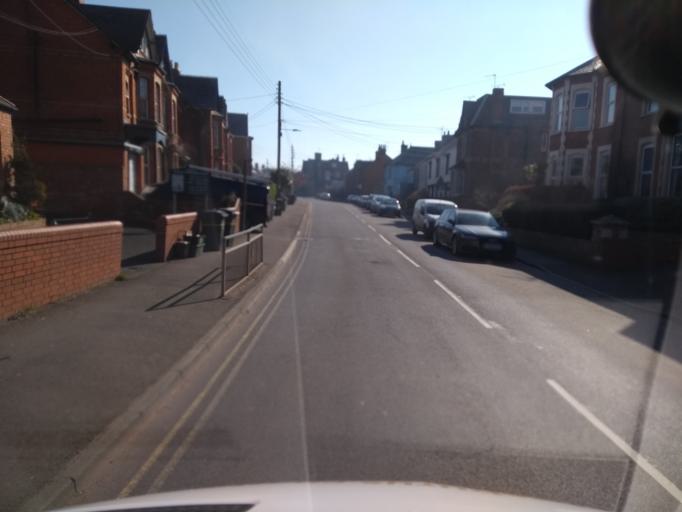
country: GB
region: England
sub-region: Somerset
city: Bishops Lydeard
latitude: 50.9808
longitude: -3.2370
